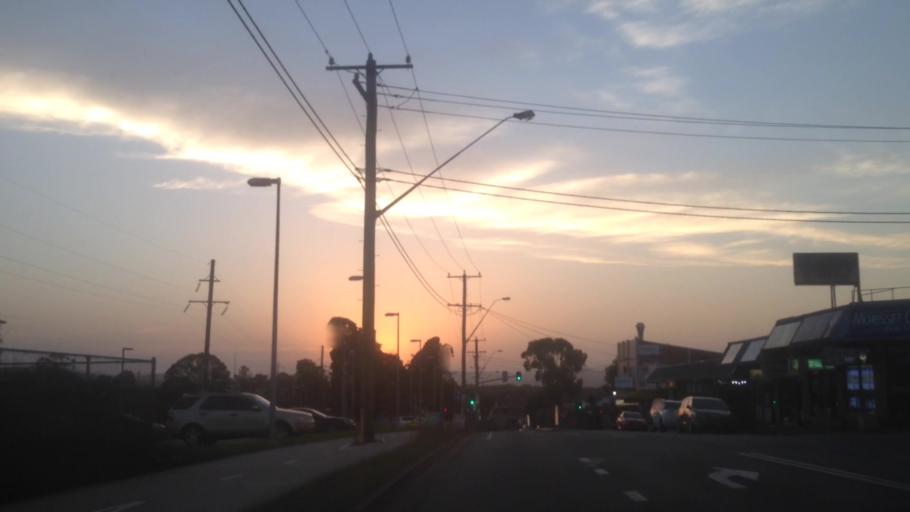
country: AU
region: New South Wales
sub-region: Lake Macquarie Shire
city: Dora Creek
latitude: -33.1075
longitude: 151.4903
